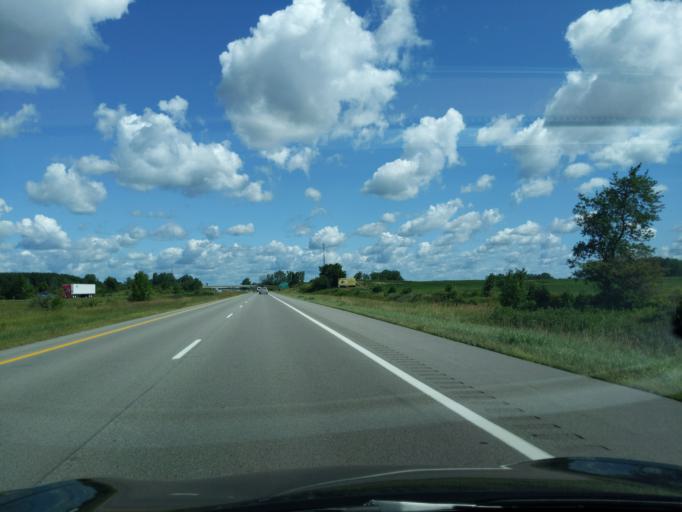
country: US
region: Michigan
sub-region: Isabella County
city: Shepherd
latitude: 43.5036
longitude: -84.6770
